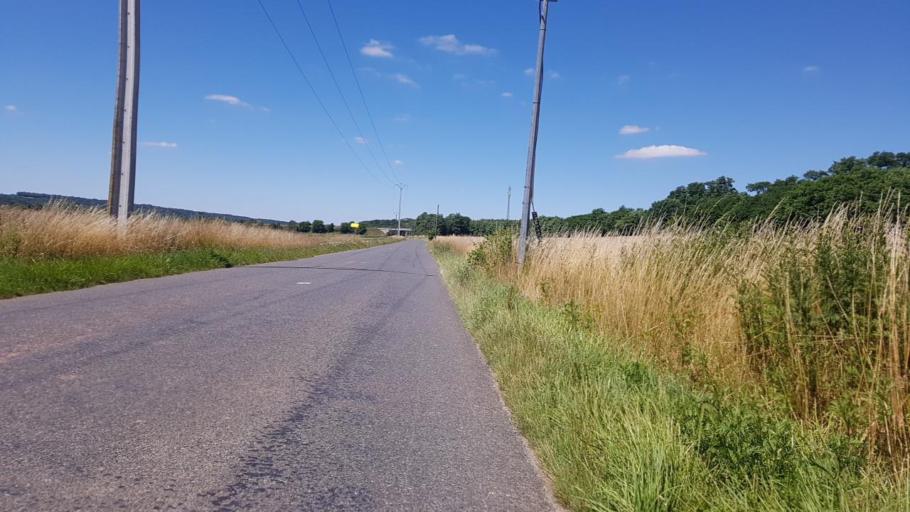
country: FR
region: Ile-de-France
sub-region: Departement de Seine-et-Marne
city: Sammeron
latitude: 48.9580
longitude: 3.0604
